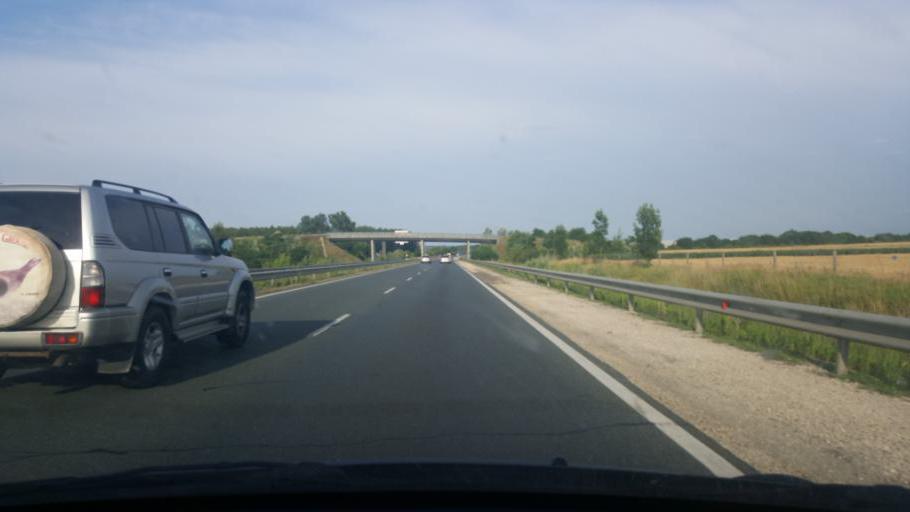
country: HU
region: Pest
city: Ullo
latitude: 47.4036
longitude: 19.3380
